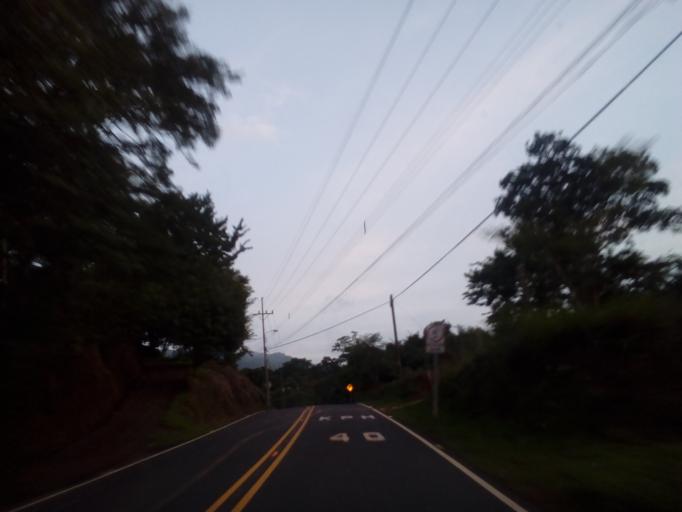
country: CR
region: Guanacaste
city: Hojancha
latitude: 10.0232
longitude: -85.5029
